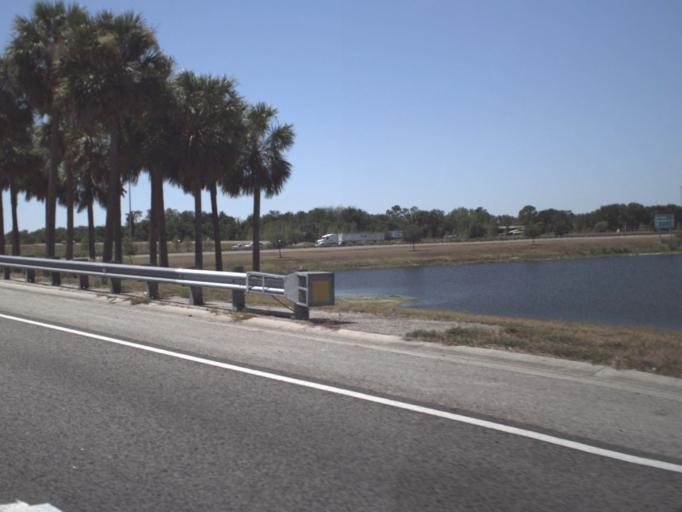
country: US
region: Florida
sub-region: Orange County
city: Belle Isle
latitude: 28.4535
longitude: -81.3097
